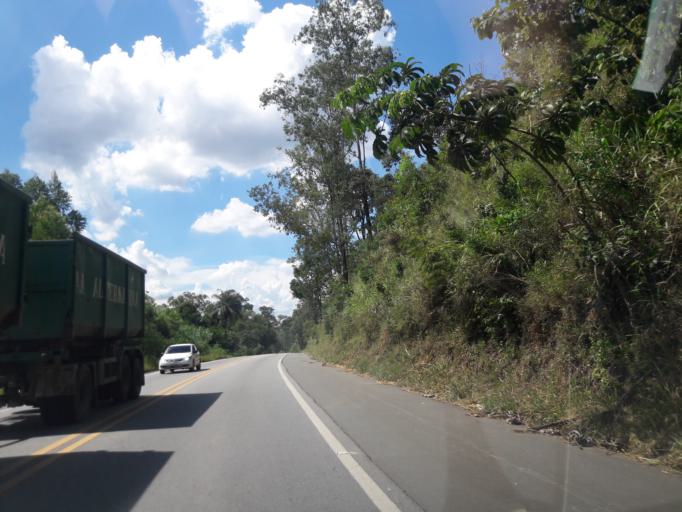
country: BR
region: Sao Paulo
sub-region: Campo Limpo Paulista
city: Campo Limpo Paulista
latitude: -23.2390
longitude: -46.7922
